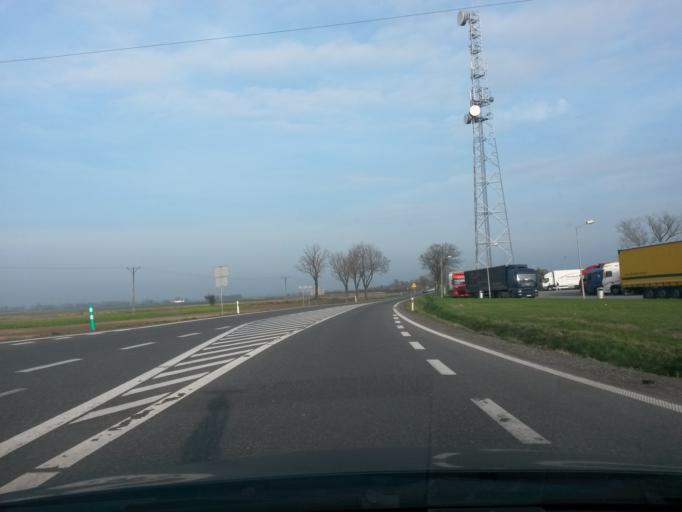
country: PL
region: Lower Silesian Voivodeship
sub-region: Powiat sredzki
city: Ciechow
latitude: 51.0376
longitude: 16.5837
